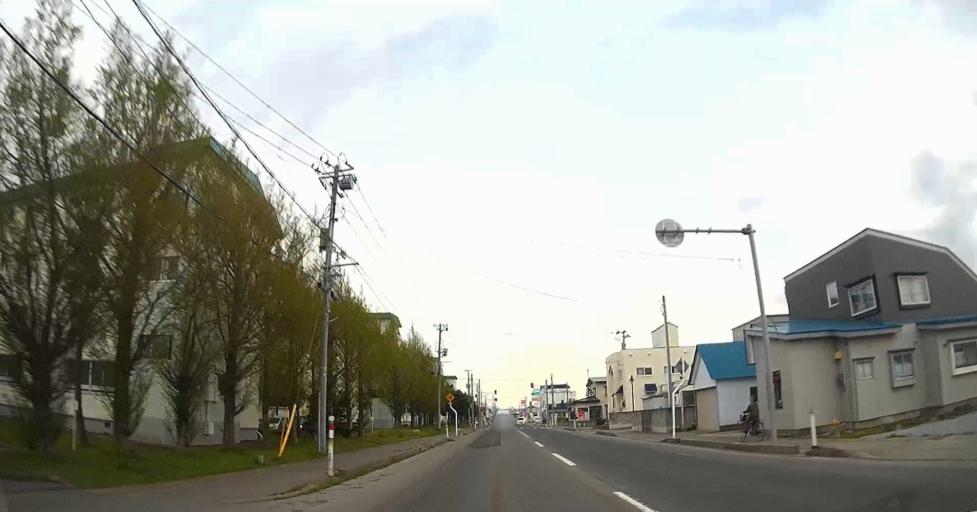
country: JP
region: Aomori
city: Aomori Shi
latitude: 40.8585
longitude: 140.6813
